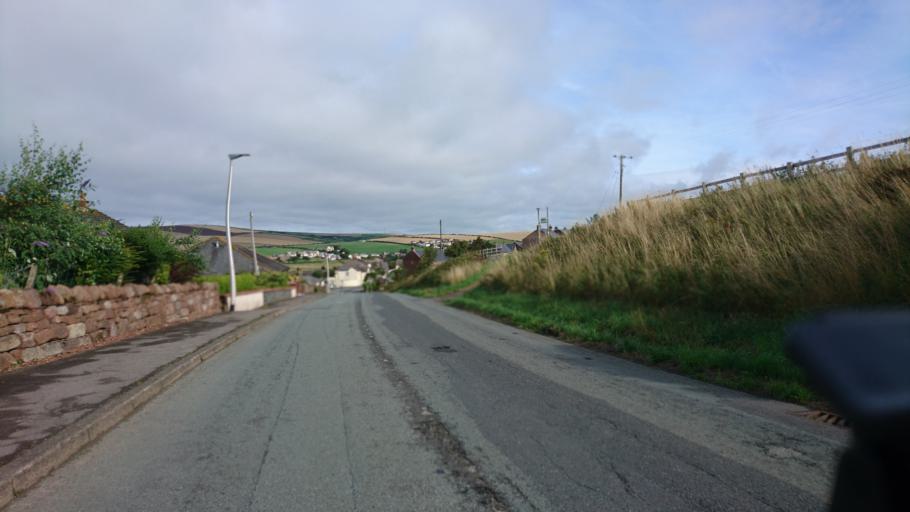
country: GB
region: England
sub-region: Cumbria
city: Saint Bees
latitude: 54.4850
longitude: -3.5880
